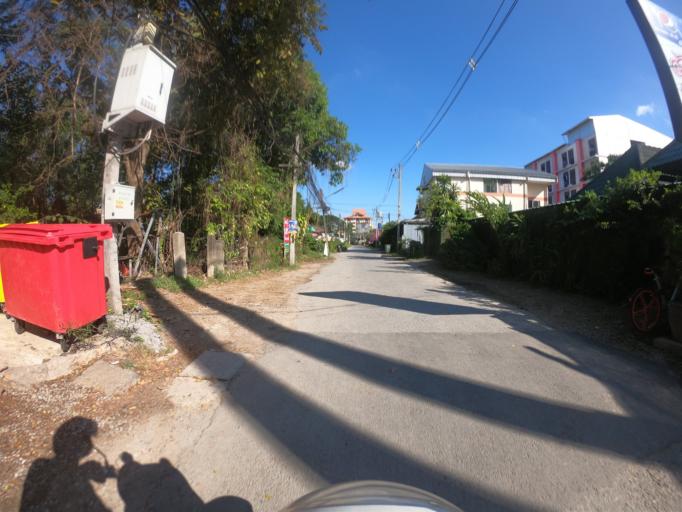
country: TH
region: Chiang Mai
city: Chiang Mai
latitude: 18.8067
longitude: 98.9767
